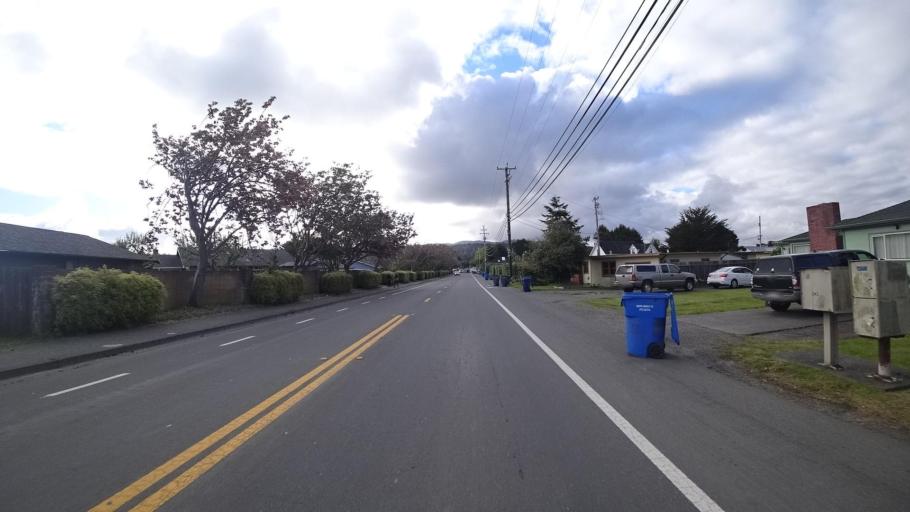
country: US
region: California
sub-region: Humboldt County
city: Arcata
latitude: 40.8914
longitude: -124.0901
